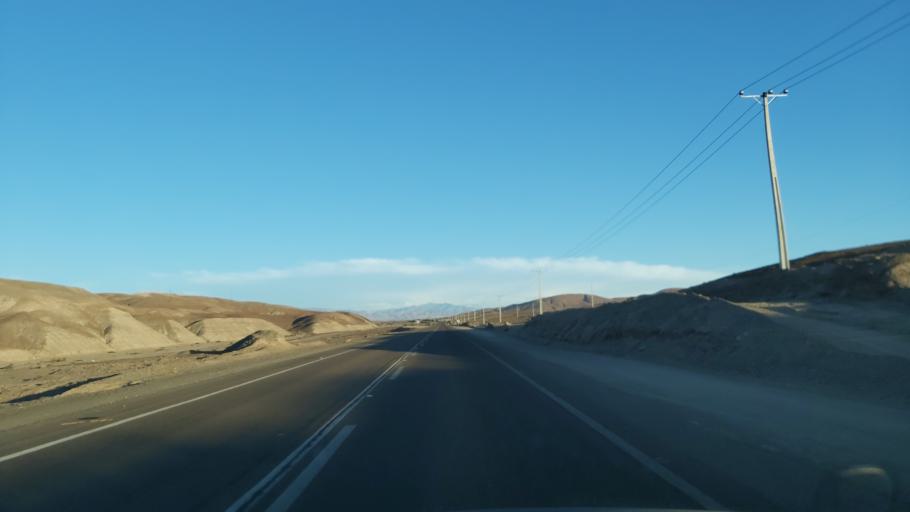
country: CL
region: Atacama
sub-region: Provincia de Chanaral
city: Diego de Almagro
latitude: -26.4206
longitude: -70.0244
